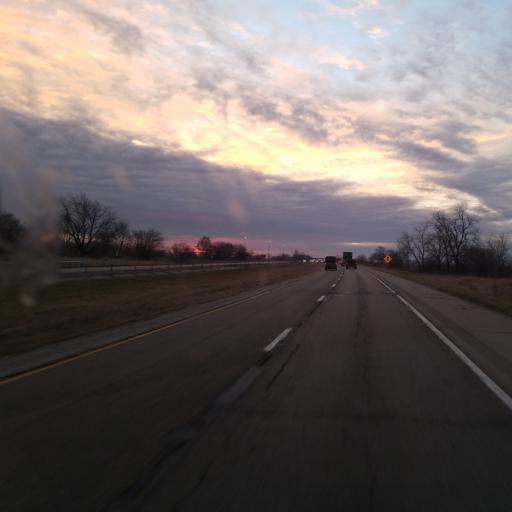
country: US
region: Illinois
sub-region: McLean County
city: Danvers
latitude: 40.5817
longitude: -89.1414
